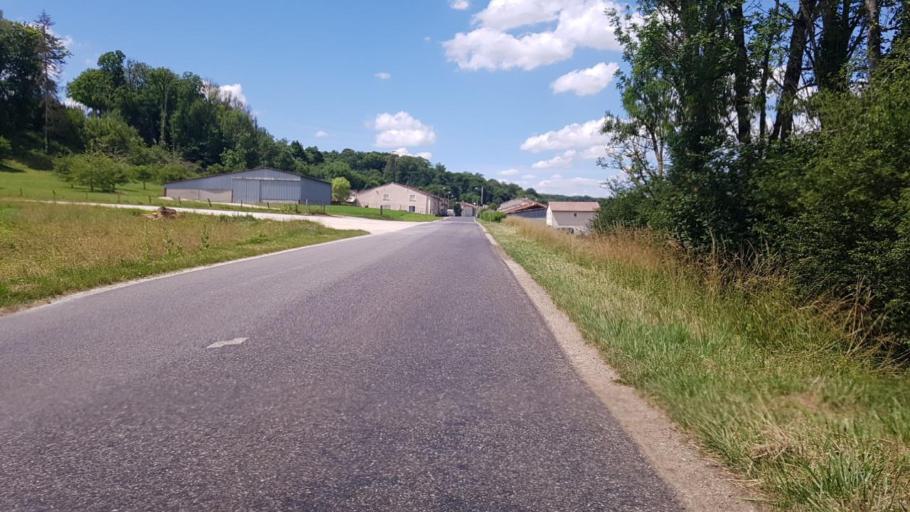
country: FR
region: Lorraine
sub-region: Departement de la Meuse
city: Gondrecourt-le-Chateau
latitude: 48.6299
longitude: 5.4715
